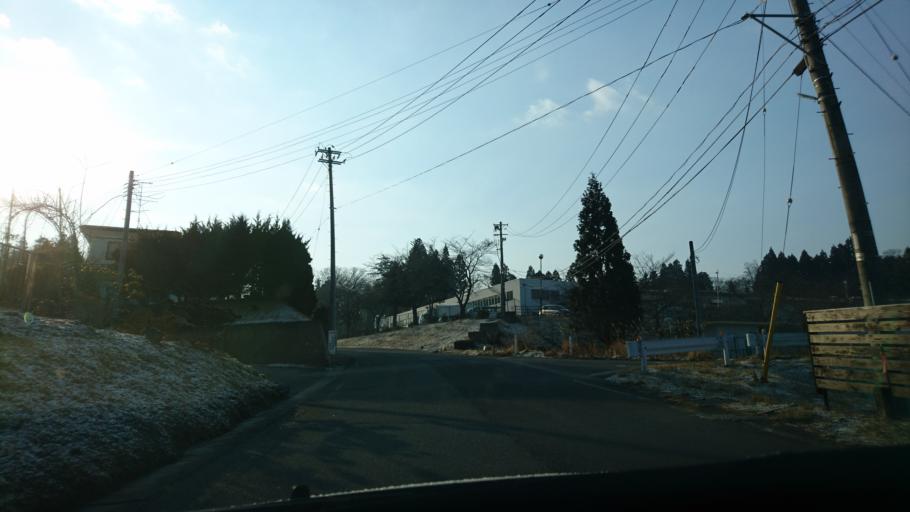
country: JP
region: Iwate
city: Ichinoseki
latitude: 38.9224
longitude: 141.3503
